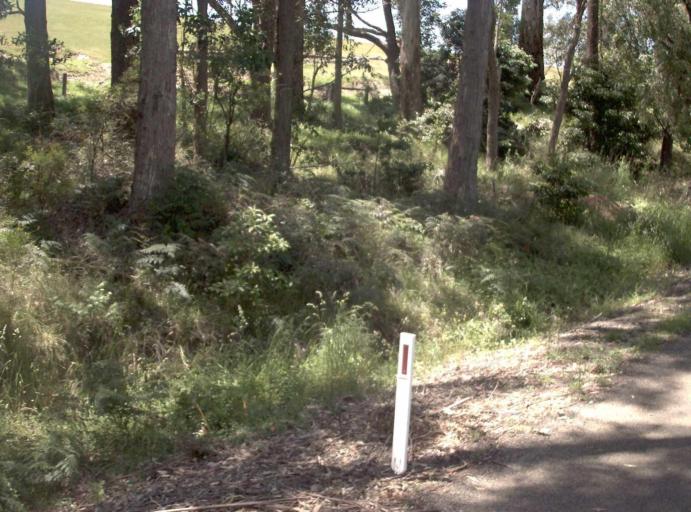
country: AU
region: Victoria
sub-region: East Gippsland
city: Lakes Entrance
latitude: -37.7067
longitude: 148.5495
